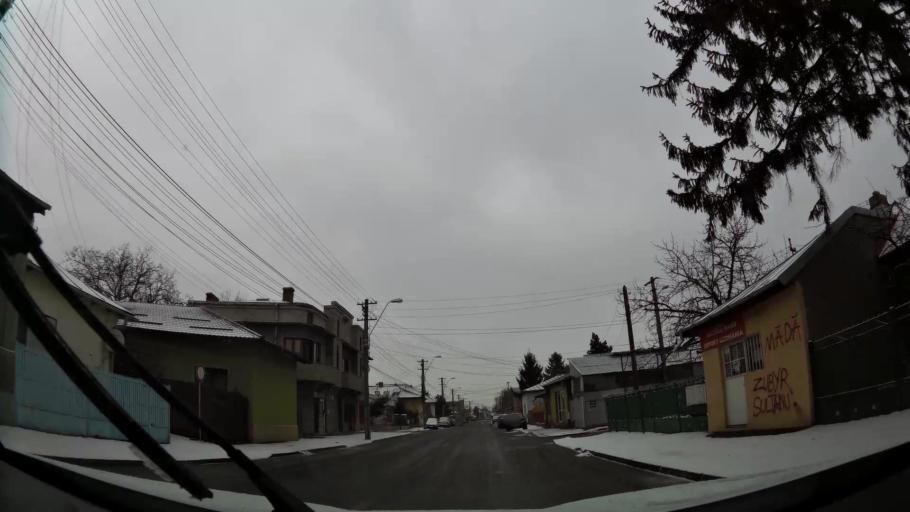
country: RO
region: Prahova
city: Ploiesti
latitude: 44.9266
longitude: 26.0164
